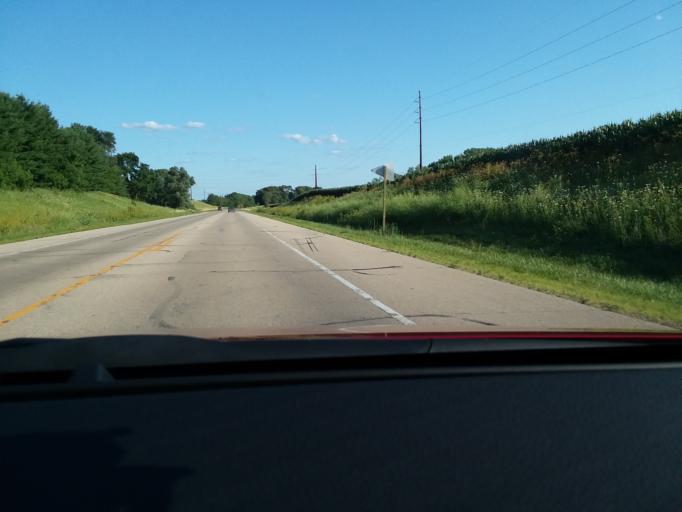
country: US
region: Wisconsin
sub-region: Dane County
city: Waunakee
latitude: 43.1699
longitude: -89.4100
